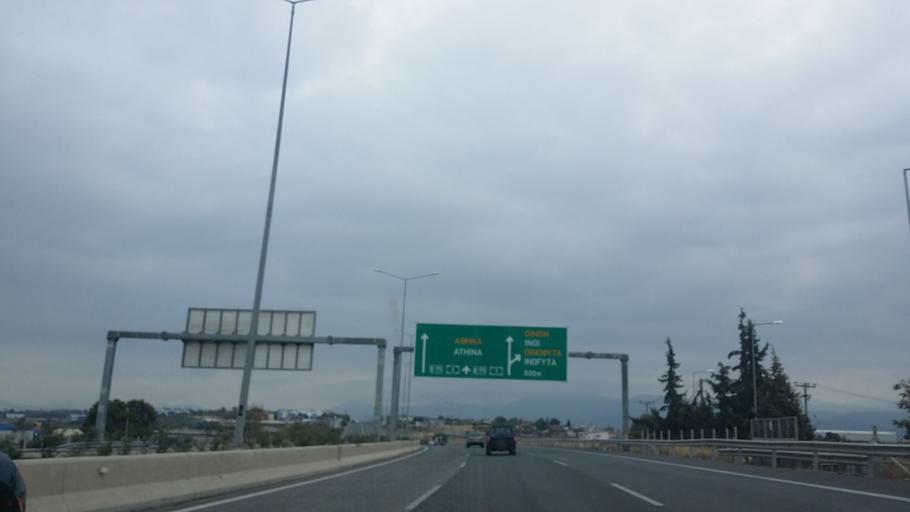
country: GR
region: Central Greece
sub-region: Nomos Voiotias
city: Schimatari
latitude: 38.3307
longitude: 23.6032
